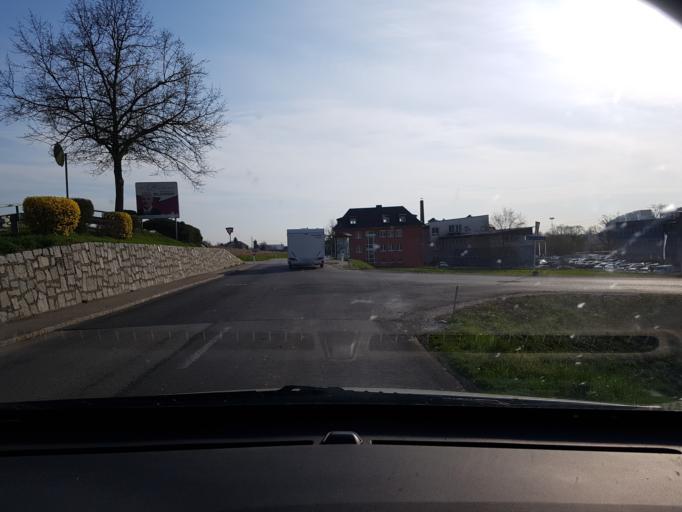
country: AT
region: Upper Austria
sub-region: Politischer Bezirk Linz-Land
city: Sankt Florian
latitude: 48.2099
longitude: 14.3943
